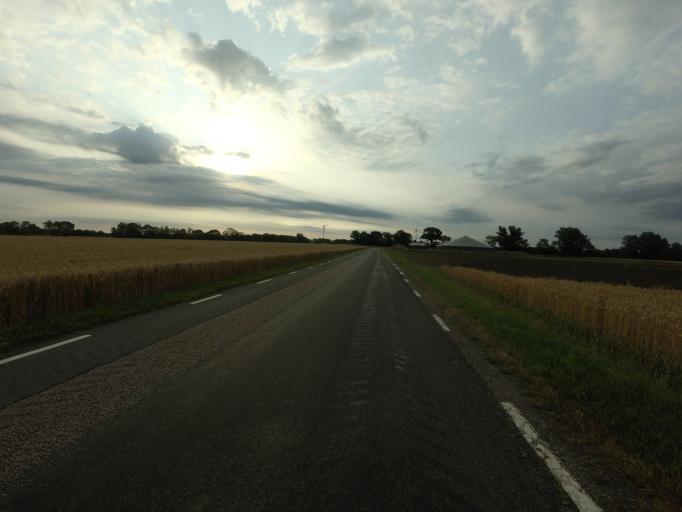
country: SE
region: Skane
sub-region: Hoganas Kommun
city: Hoganas
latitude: 56.1527
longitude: 12.6384
